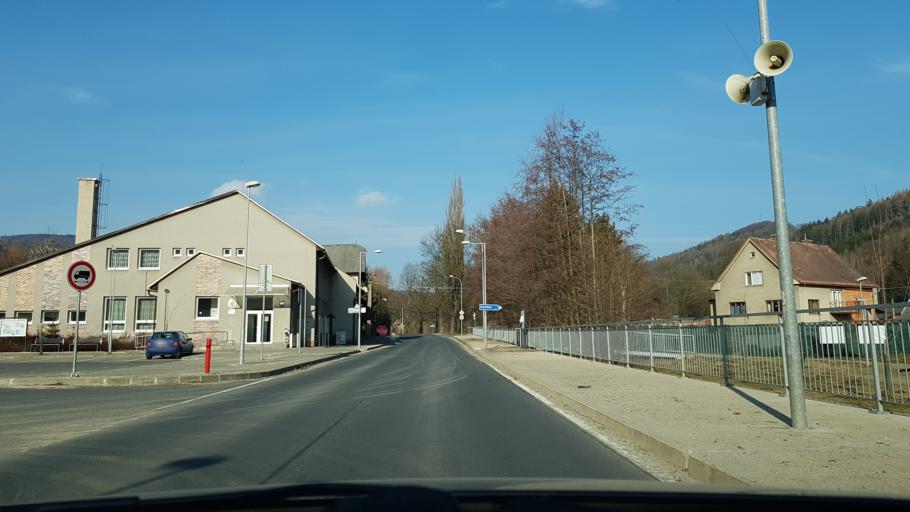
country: CZ
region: Olomoucky
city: Dolni Bohdikov
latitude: 50.0269
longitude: 16.8985
